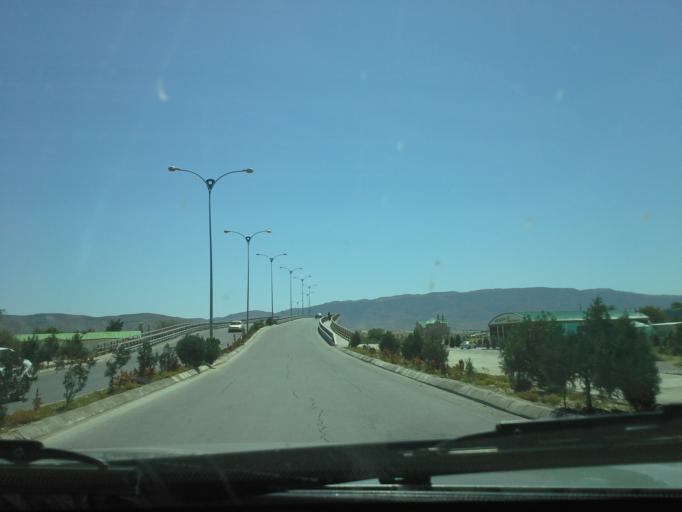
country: TM
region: Balkan
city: Serdar
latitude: 38.9814
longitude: 56.2791
